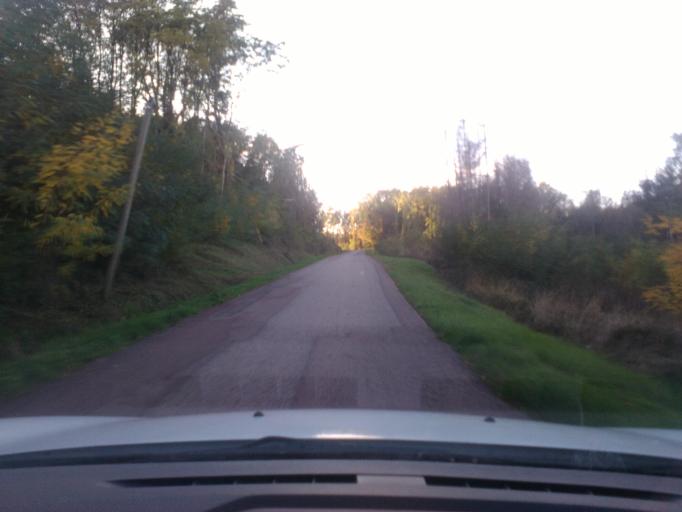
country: FR
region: Lorraine
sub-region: Departement des Vosges
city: Vincey
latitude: 48.3312
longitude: 6.3187
